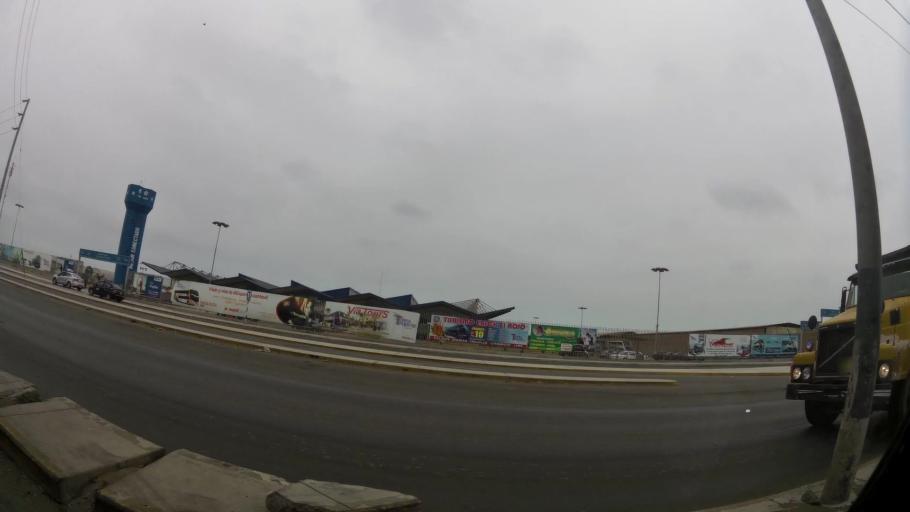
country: PE
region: La Libertad
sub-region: Provincia de Trujillo
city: Buenos Aires
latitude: -8.1366
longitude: -79.0168
